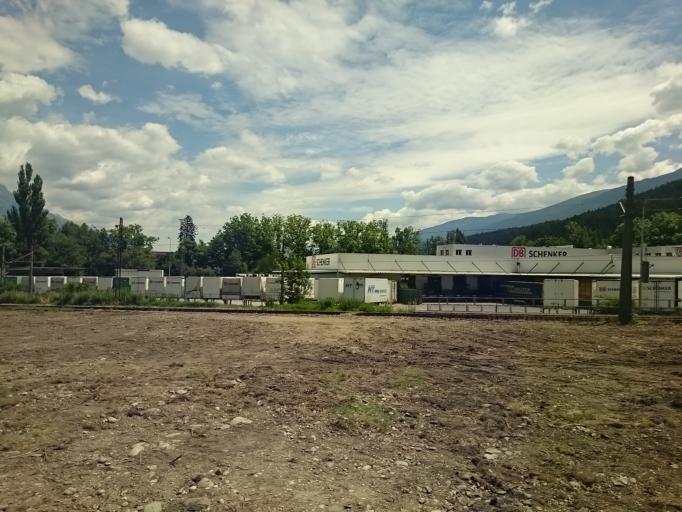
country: AT
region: Tyrol
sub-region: Innsbruck Stadt
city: Innsbruck
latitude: 47.2551
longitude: 11.4021
